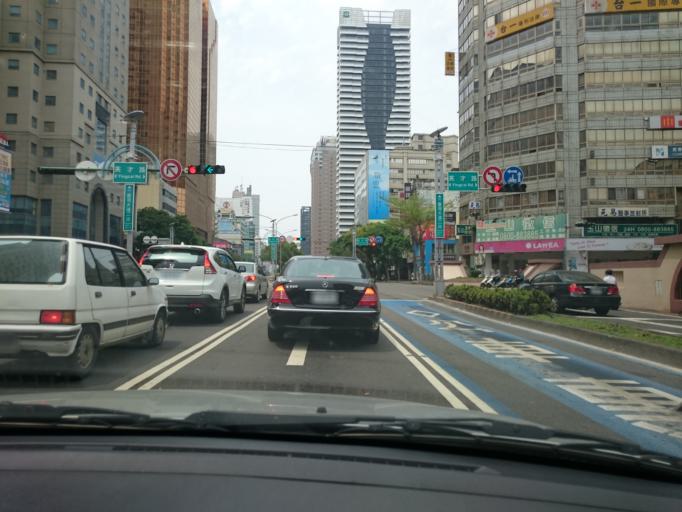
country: TW
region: Taiwan
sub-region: Taichung City
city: Taichung
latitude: 24.1531
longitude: 120.6671
